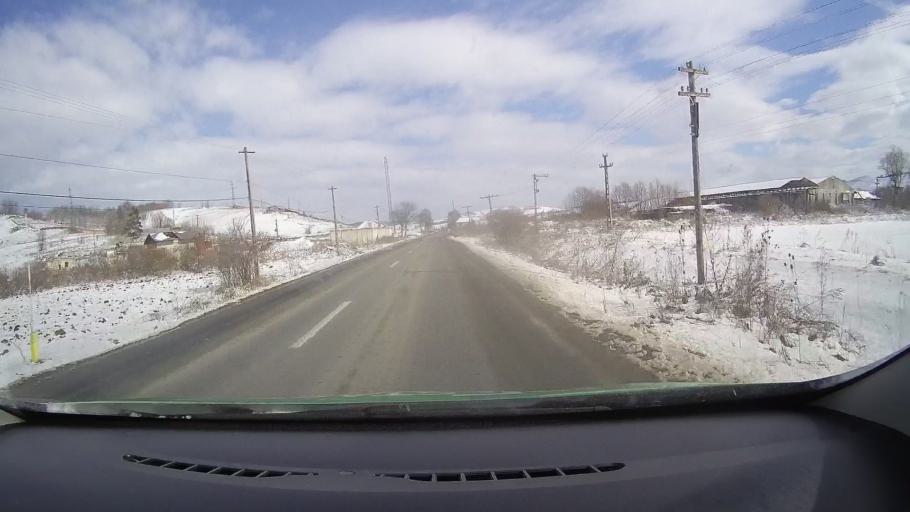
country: RO
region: Sibiu
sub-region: Oras Agnita
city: Agnita
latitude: 45.9644
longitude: 24.5859
